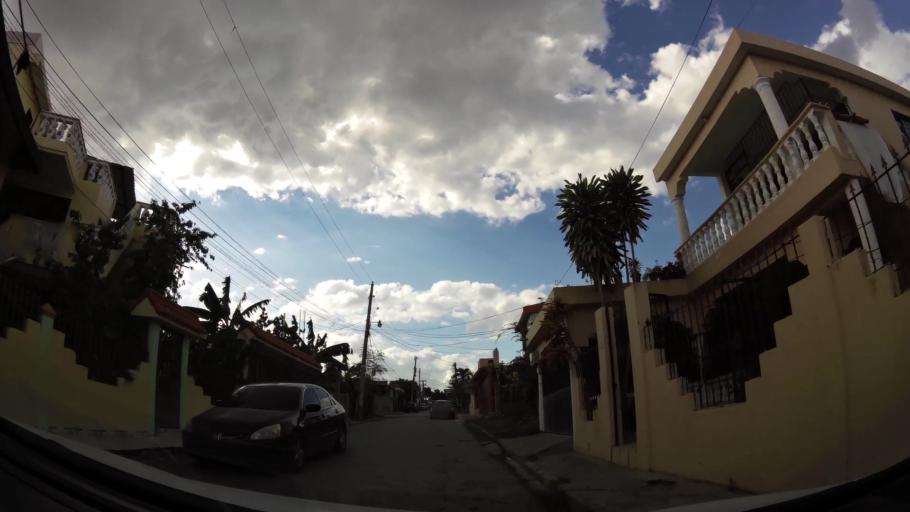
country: DO
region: Nacional
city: Ensanche Luperon
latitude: 18.5611
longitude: -69.9044
